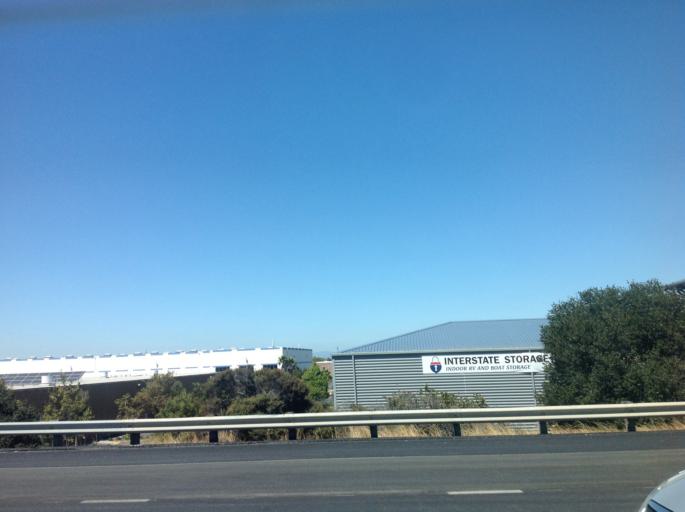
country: US
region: California
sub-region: Contra Costa County
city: Richmond
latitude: 37.9272
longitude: -122.3729
